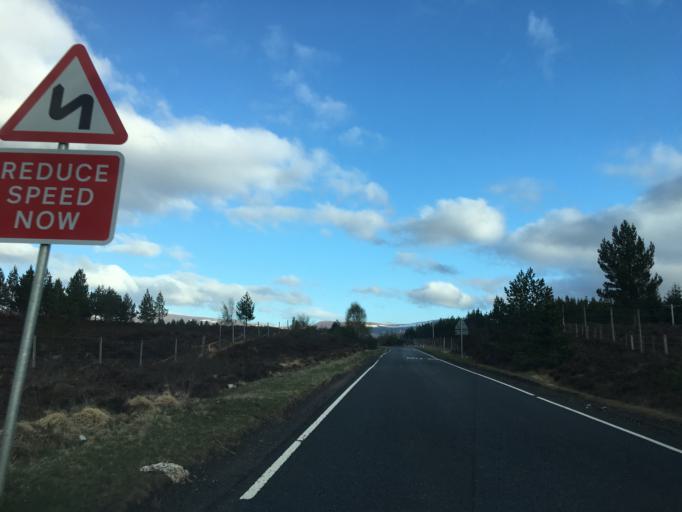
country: GB
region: Scotland
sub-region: Highland
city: Kingussie
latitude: 56.9868
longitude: -4.2424
